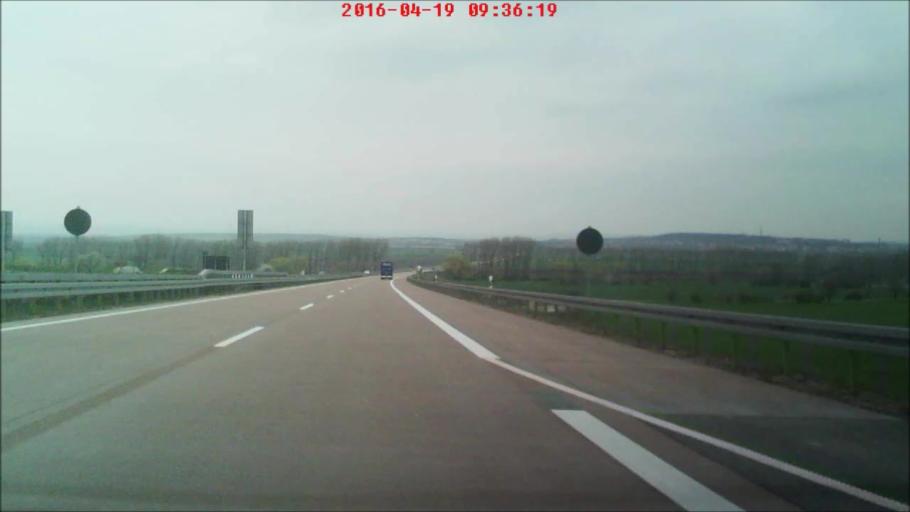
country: DE
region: Thuringia
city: Reinsdorf
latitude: 51.3338
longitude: 11.2540
